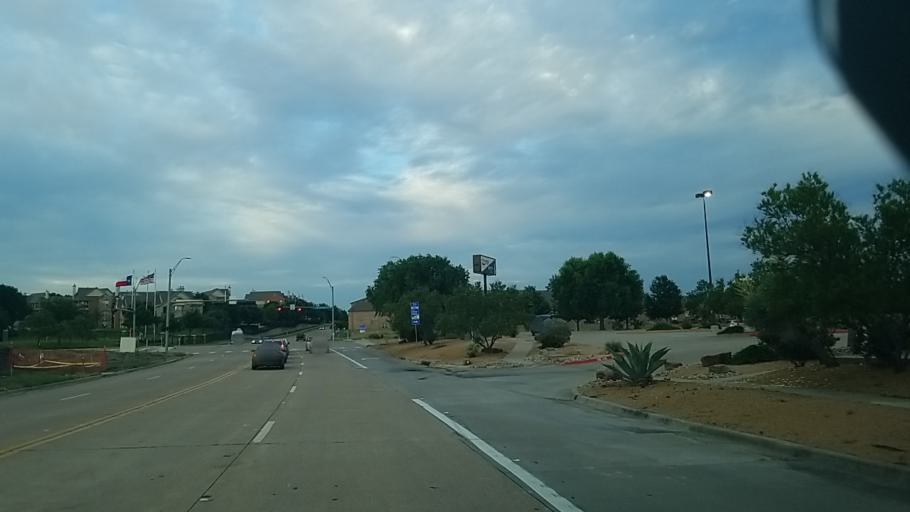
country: US
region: Texas
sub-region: Denton County
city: Lewisville
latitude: 32.9985
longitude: -96.9775
